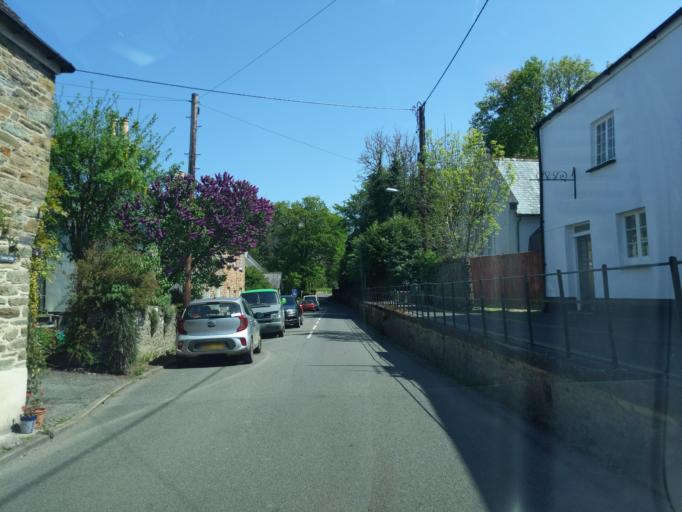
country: GB
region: England
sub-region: Cornwall
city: Pillaton
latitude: 50.3973
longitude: -4.3141
